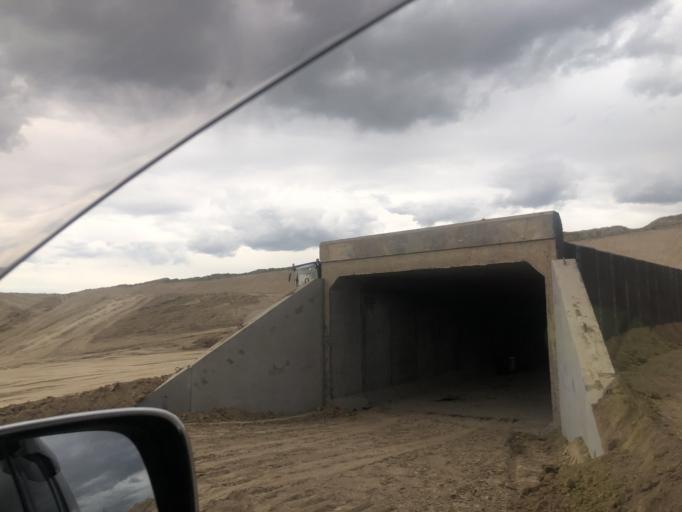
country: KG
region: Chuy
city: Bystrovka
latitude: 43.3252
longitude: 75.8180
